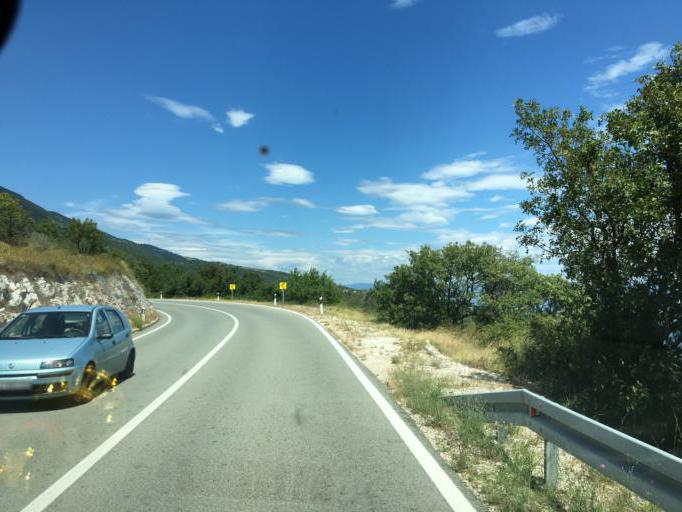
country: HR
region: Istarska
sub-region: Grad Labin
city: Rabac
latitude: 45.1425
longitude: 14.2130
